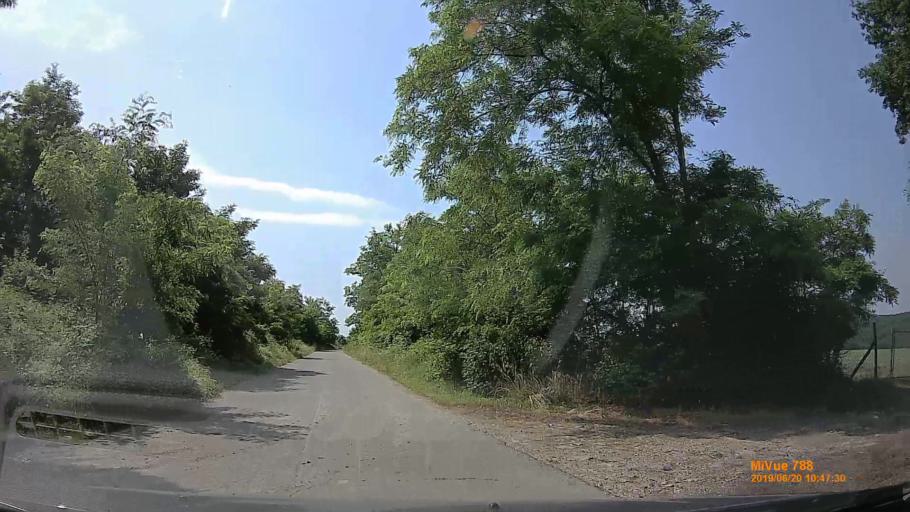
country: HU
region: Baranya
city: Hidas
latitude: 46.1751
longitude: 18.5823
